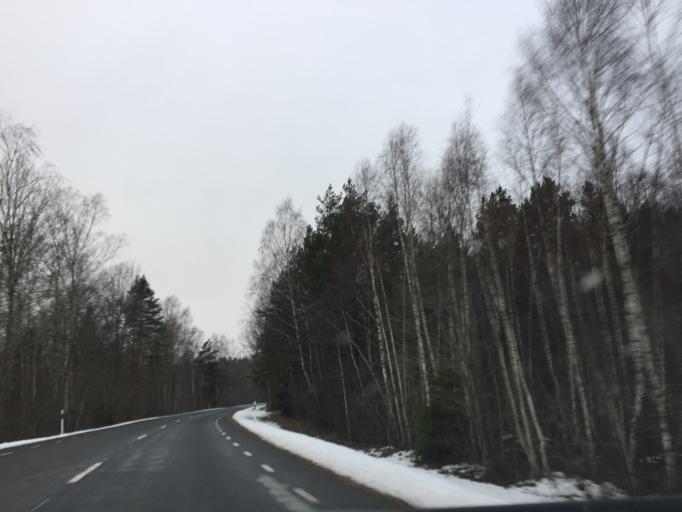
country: EE
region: Saare
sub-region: Kuressaare linn
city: Kuressaare
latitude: 58.5534
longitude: 22.3209
